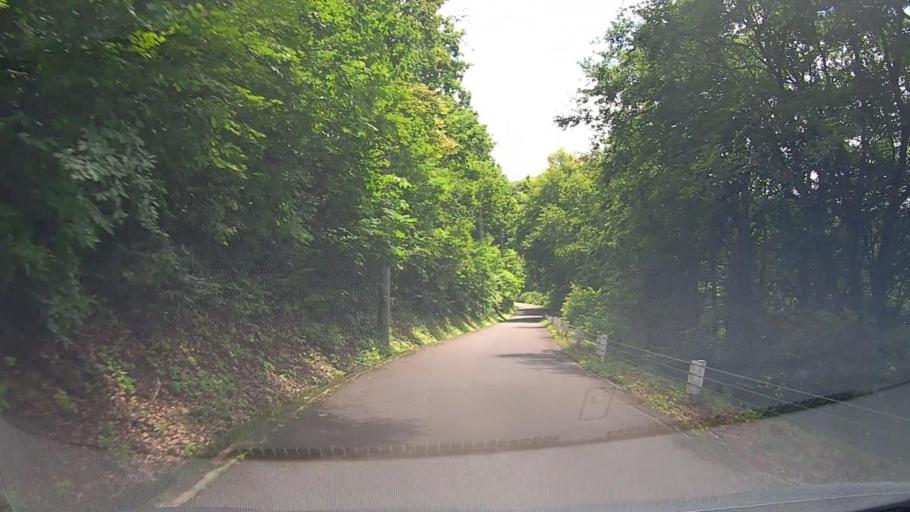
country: JP
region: Nagano
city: Iiyama
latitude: 36.9325
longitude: 138.4674
